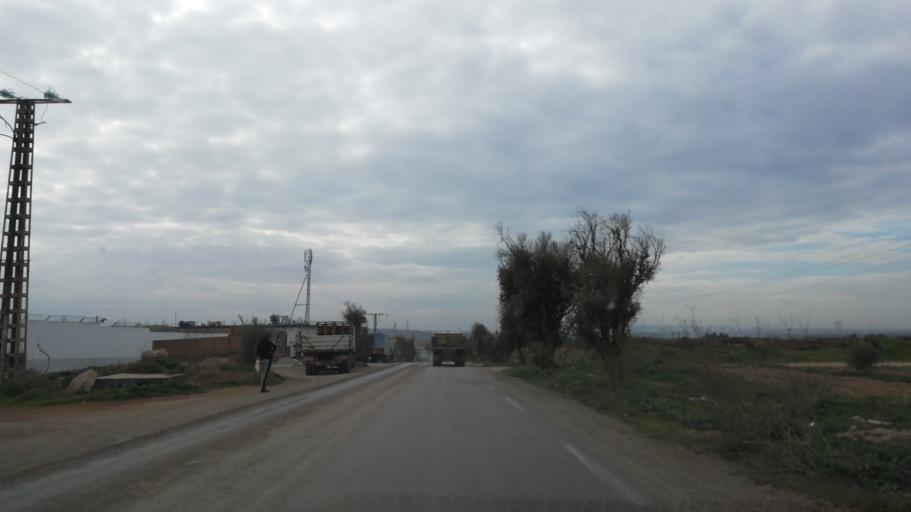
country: DZ
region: Oran
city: Ain el Bya
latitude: 35.7845
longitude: -0.3438
